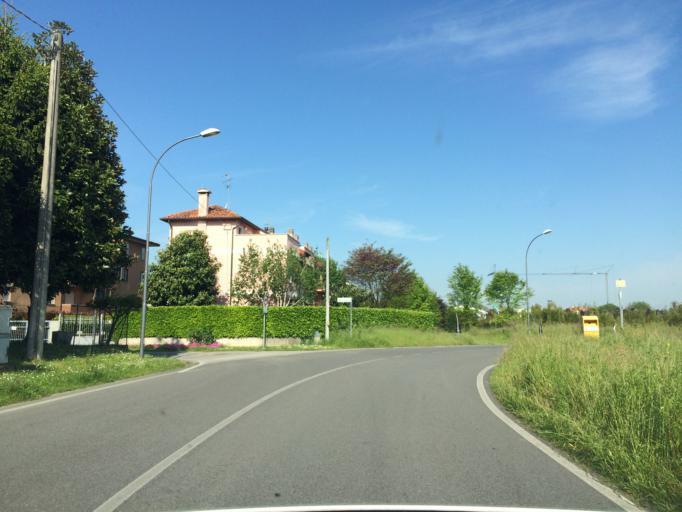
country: IT
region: Veneto
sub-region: Provincia di Padova
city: Abano Terme
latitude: 45.3528
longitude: 11.7939
